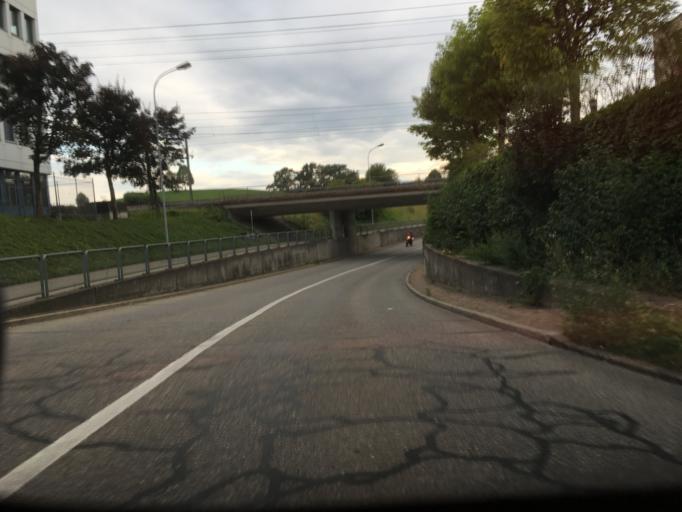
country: CH
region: Zurich
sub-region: Bezirk Uster
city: Duebendorf / Sonnenberg
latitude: 47.3940
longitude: 8.6401
